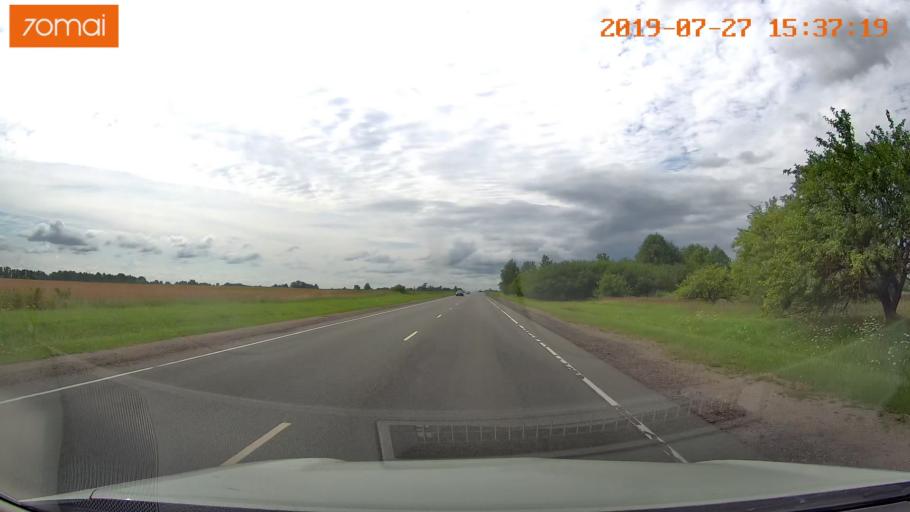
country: RU
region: Kaliningrad
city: Gusev
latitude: 54.6102
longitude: 22.3453
